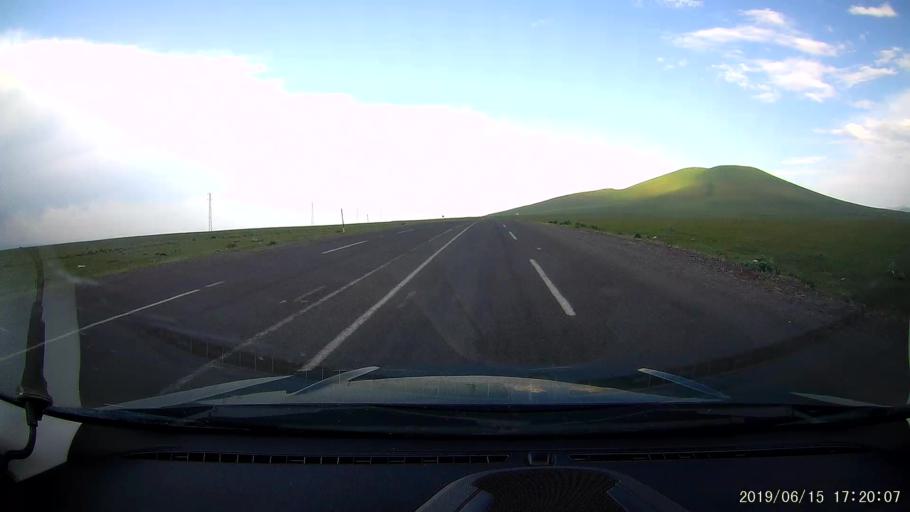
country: TR
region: Kars
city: Kars
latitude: 40.6161
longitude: 43.2939
